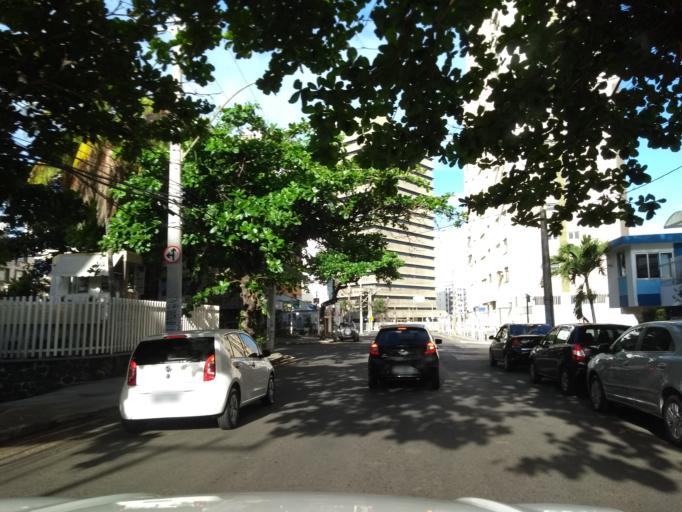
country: BR
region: Bahia
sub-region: Salvador
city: Salvador
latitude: -13.0019
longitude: -38.4558
